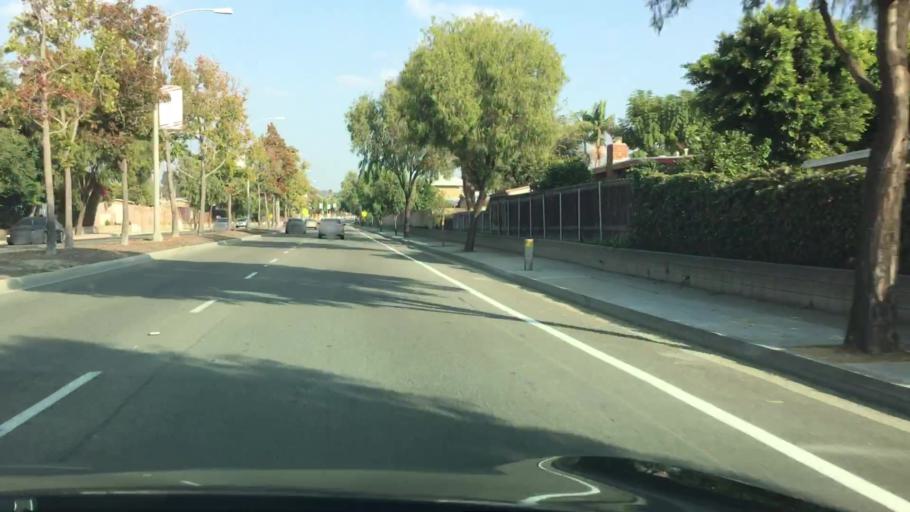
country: US
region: California
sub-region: Los Angeles County
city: La Mirada
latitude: 33.8988
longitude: -118.0045
